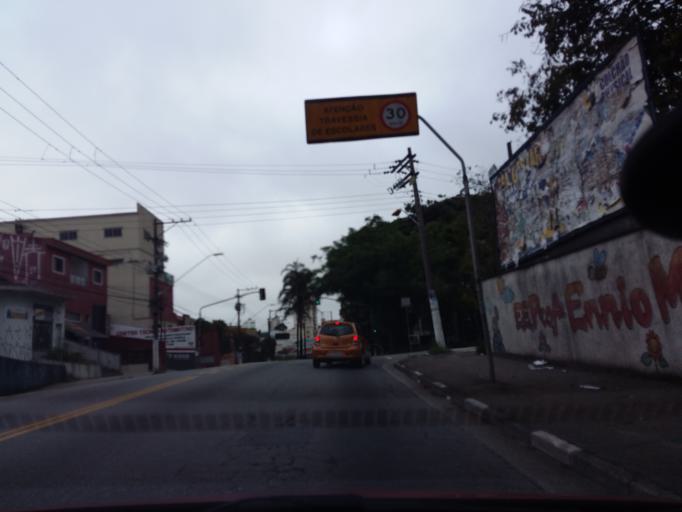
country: BR
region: Sao Paulo
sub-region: Santo Andre
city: Santo Andre
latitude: -23.6610
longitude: -46.5508
